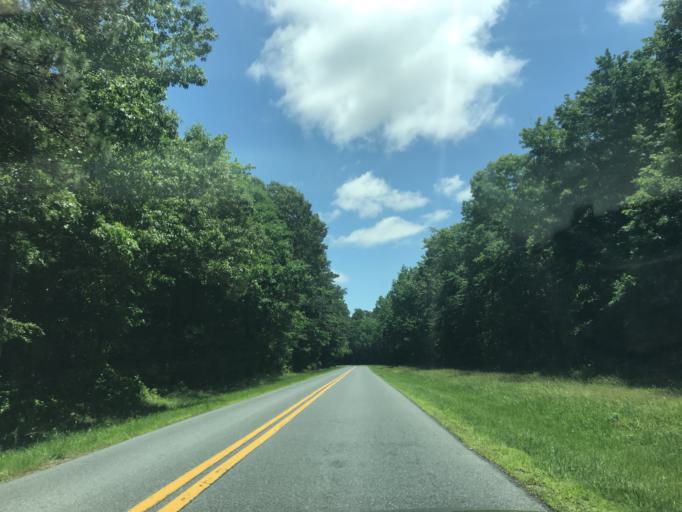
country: US
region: Maryland
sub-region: Caroline County
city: Federalsburg
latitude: 38.7408
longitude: -75.7109
